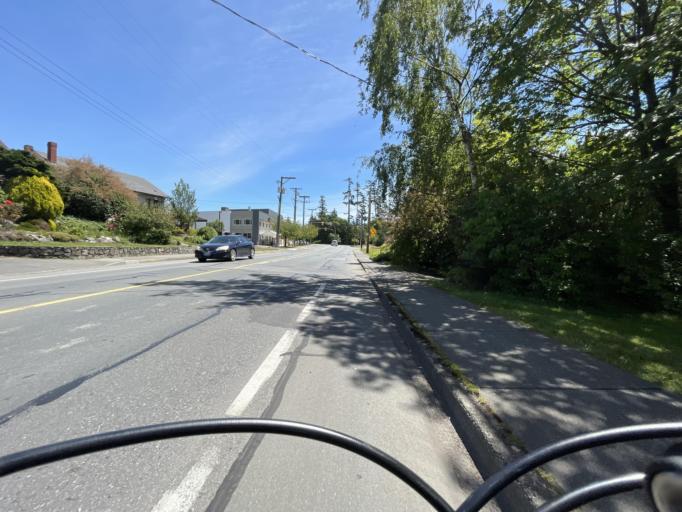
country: CA
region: British Columbia
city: Victoria
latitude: 48.4480
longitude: -123.4019
